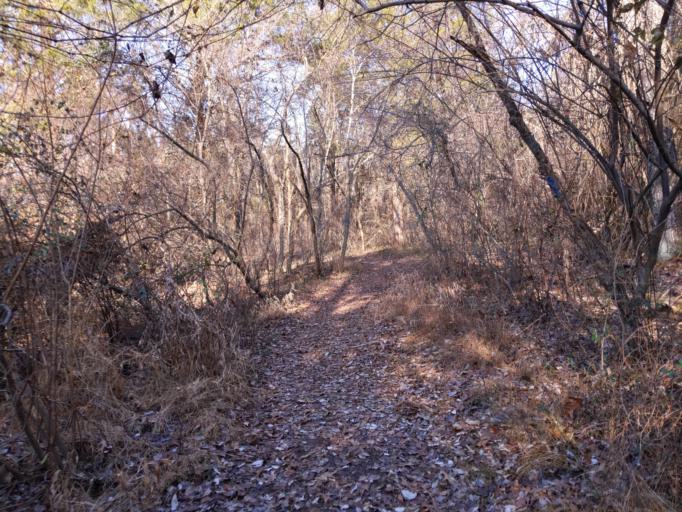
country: US
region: Virginia
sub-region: Loudoun County
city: Dulles Town Center
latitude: 39.0206
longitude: -77.4072
